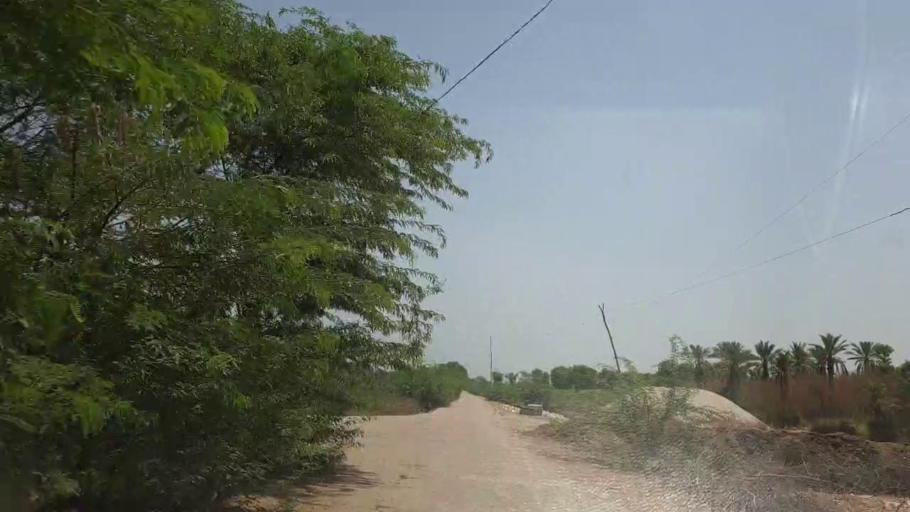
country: PK
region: Sindh
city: Kot Diji
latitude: 27.2867
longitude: 68.6424
